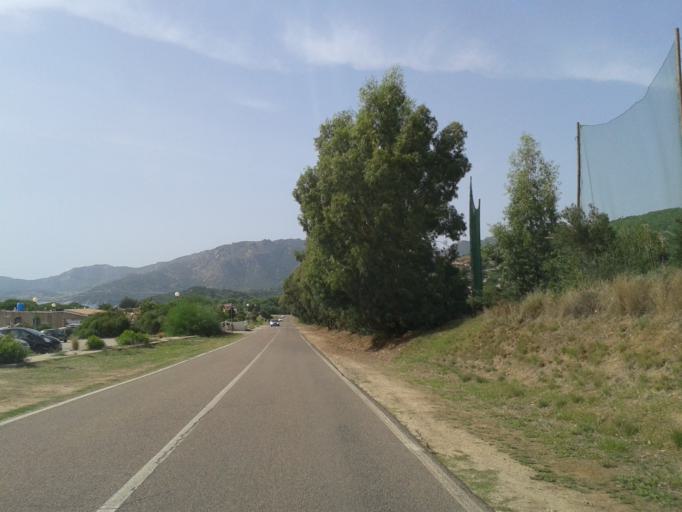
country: IT
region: Sardinia
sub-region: Provincia di Cagliari
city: Villasimius
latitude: 39.1281
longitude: 9.5146
